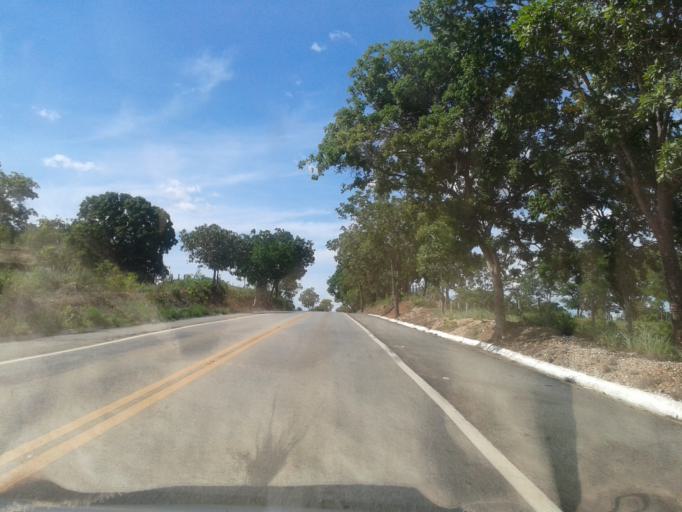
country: BR
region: Goias
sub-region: Itapuranga
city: Itapuranga
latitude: -15.4260
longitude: -50.3749
